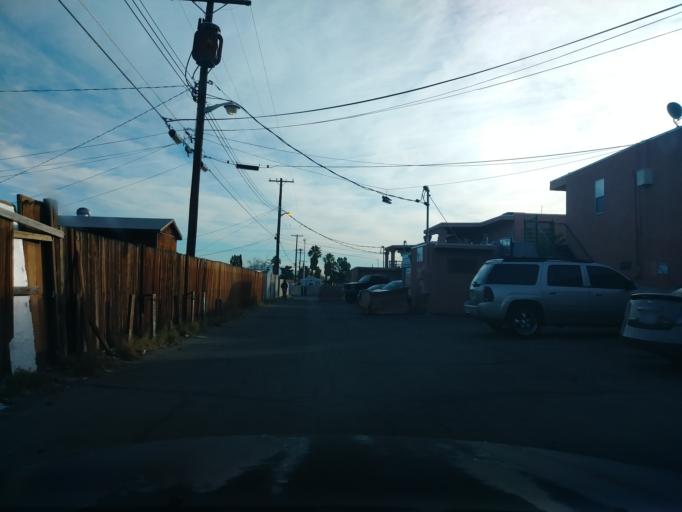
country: US
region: Nevada
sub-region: Clark County
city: Spring Valley
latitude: 36.1611
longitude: -115.2320
